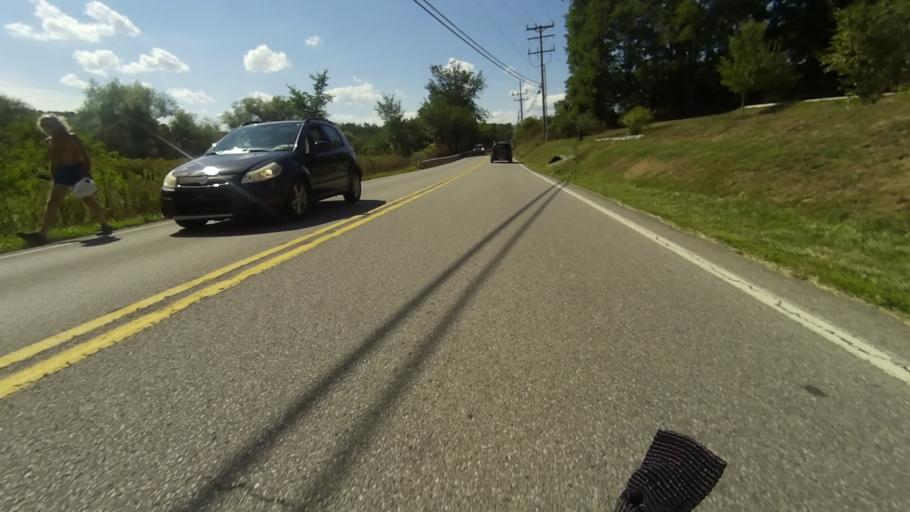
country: US
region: Pennsylvania
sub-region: Blair County
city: Greenwood
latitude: 40.5667
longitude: -78.3410
